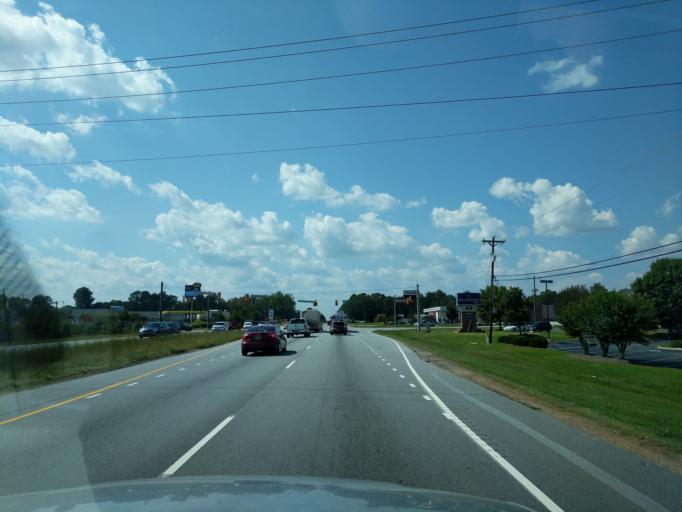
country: US
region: South Carolina
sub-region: Anderson County
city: Powdersville
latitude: 34.7896
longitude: -82.4853
